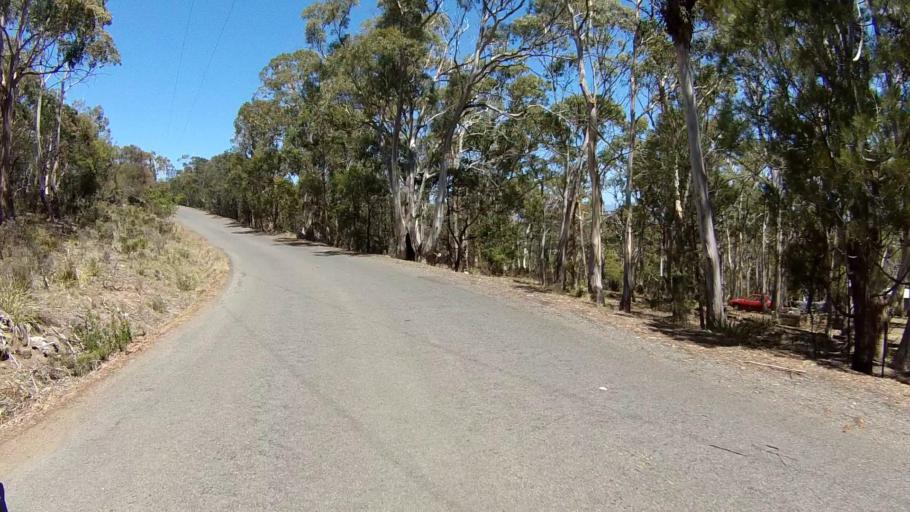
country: AU
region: Tasmania
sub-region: Clarence
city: Cambridge
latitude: -42.8454
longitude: 147.4322
